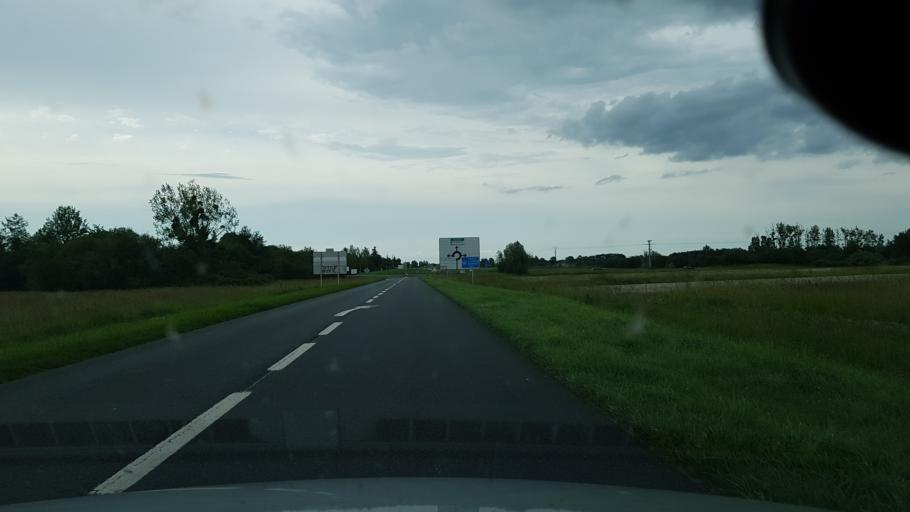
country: FR
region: Centre
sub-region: Departement du Loir-et-Cher
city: Chatillon-sur-Cher
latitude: 47.3187
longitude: 1.4979
